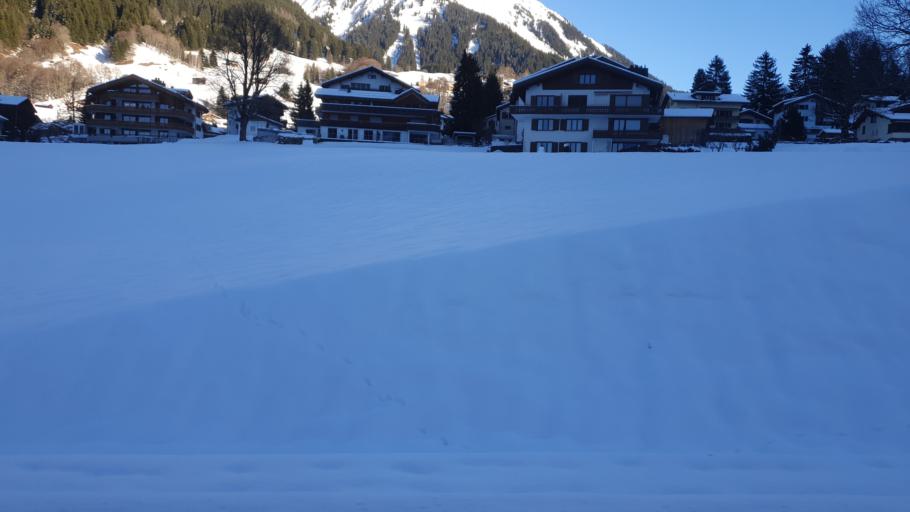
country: CH
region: Grisons
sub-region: Praettigau/Davos District
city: Klosters Serneus
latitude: 46.8756
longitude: 9.8771
